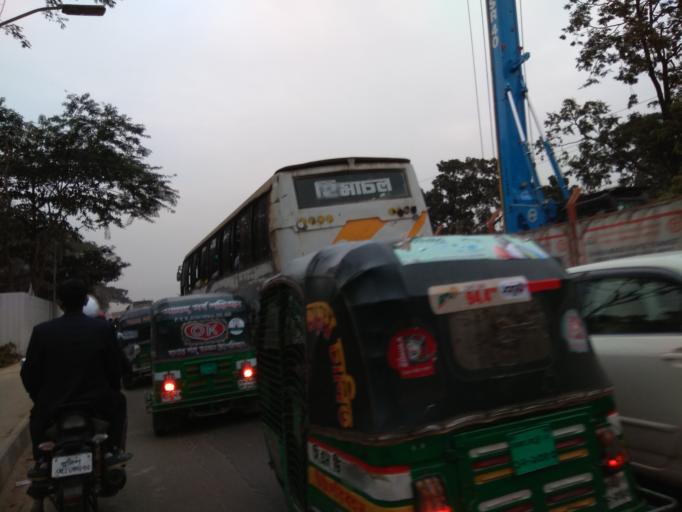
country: BD
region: Dhaka
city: Azimpur
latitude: 23.7740
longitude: 90.3813
